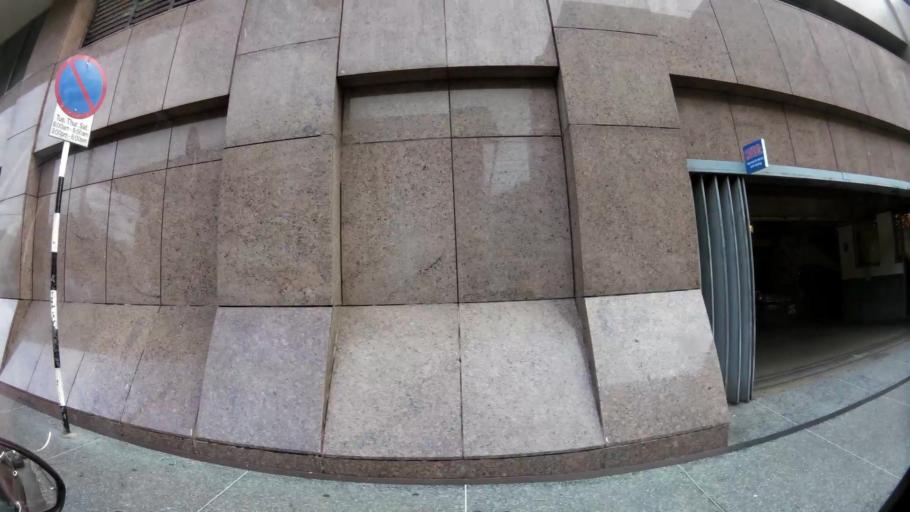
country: TT
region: San Juan/Laventille
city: Laventille
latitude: 10.6566
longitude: -61.5085
